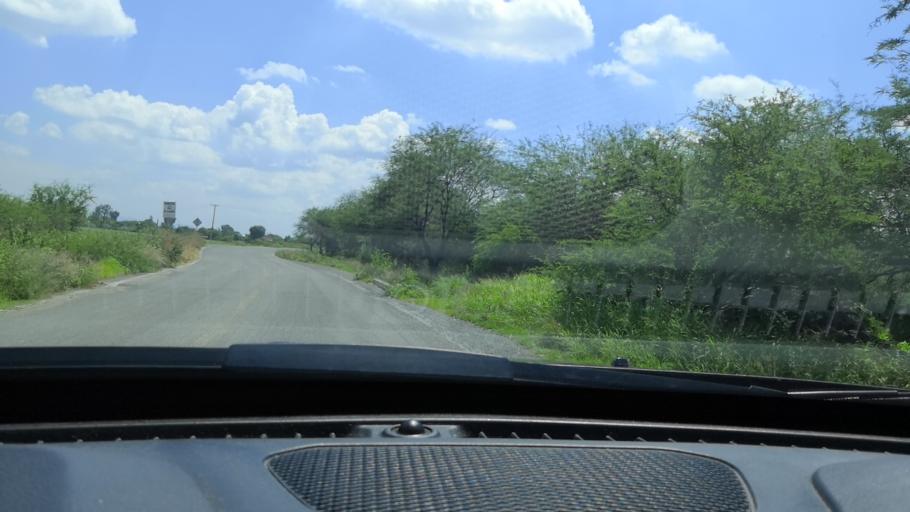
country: MX
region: Guanajuato
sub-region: Leon
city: Plan Guanajuato (La Sandia)
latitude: 20.9496
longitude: -101.6073
